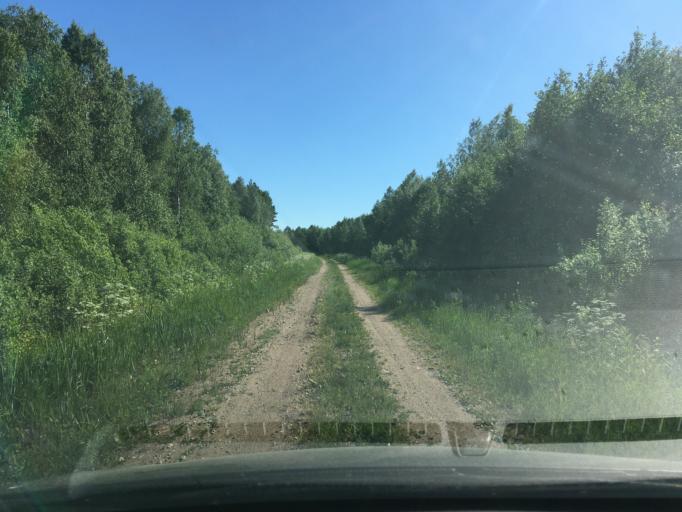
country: EE
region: Laeaene
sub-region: Lihula vald
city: Lihula
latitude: 58.6293
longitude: 23.7362
